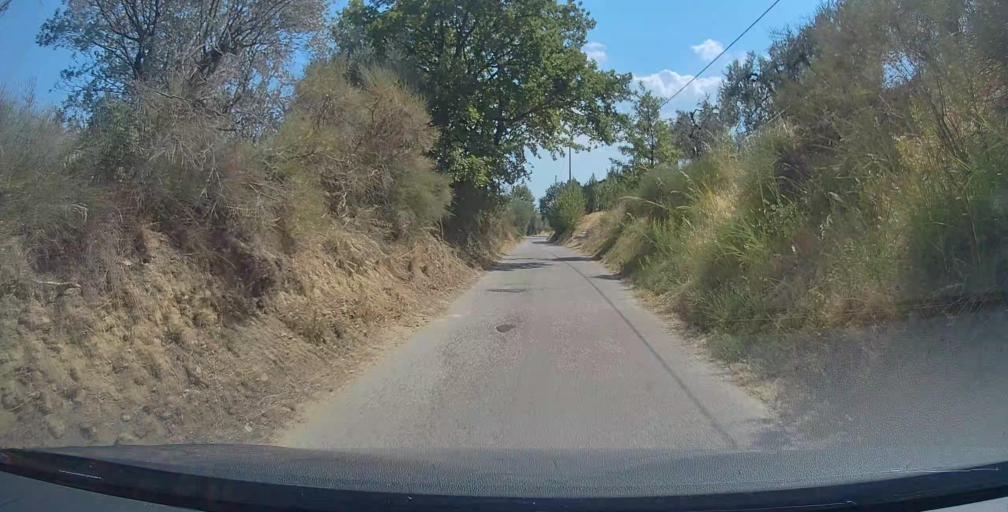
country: IT
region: Umbria
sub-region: Provincia di Terni
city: Calvi dell'Umbria
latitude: 42.3790
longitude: 12.5681
